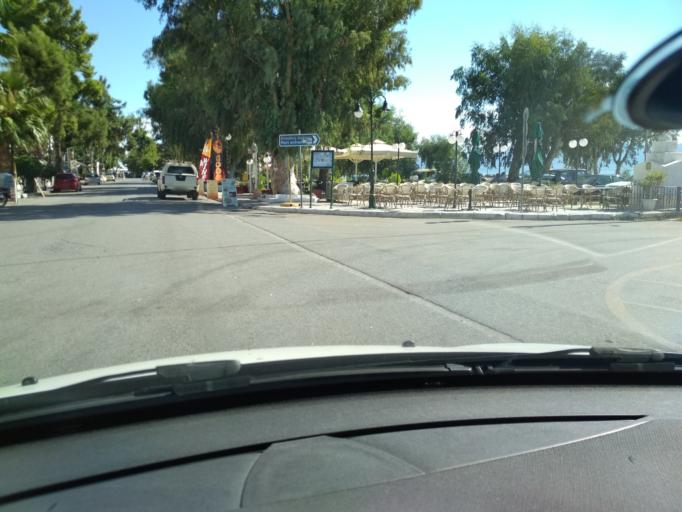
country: GR
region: Central Greece
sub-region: Nomos Evvoias
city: Oreoi
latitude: 38.8575
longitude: 23.0416
